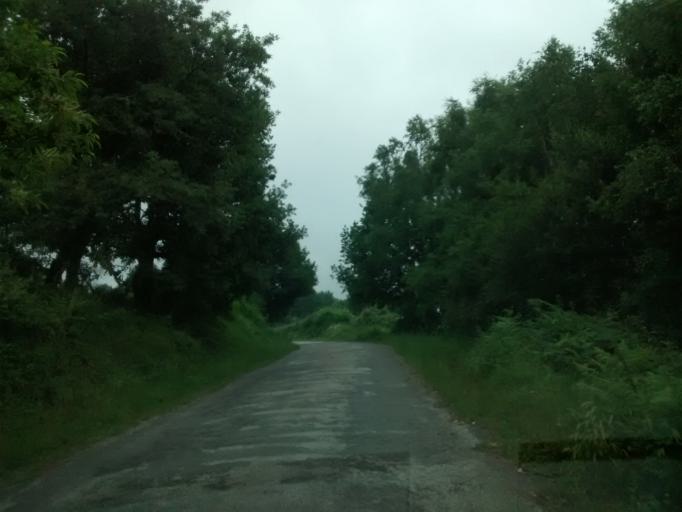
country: ES
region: Galicia
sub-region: Provincia de Ourense
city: Castro Caldelas
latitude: 42.3931
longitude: -7.3963
